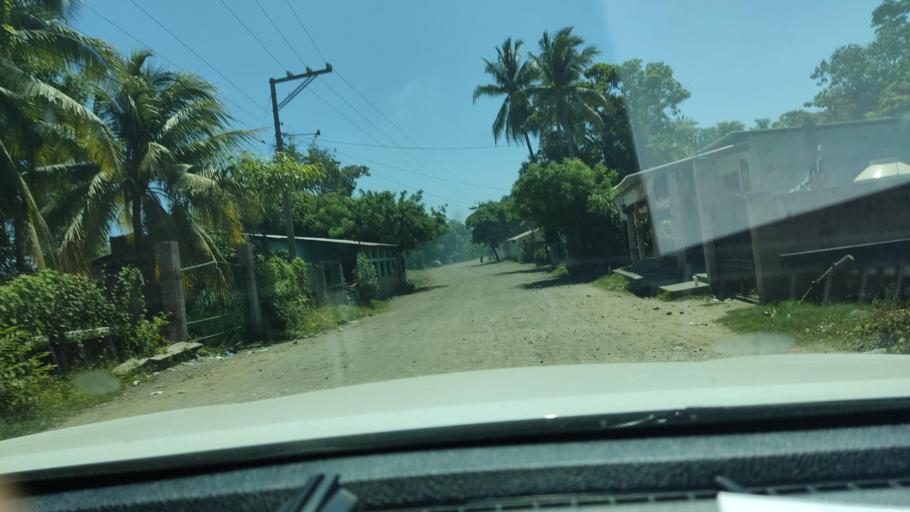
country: SV
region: Ahuachapan
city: San Francisco Menendez
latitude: 13.7647
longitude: -90.1576
